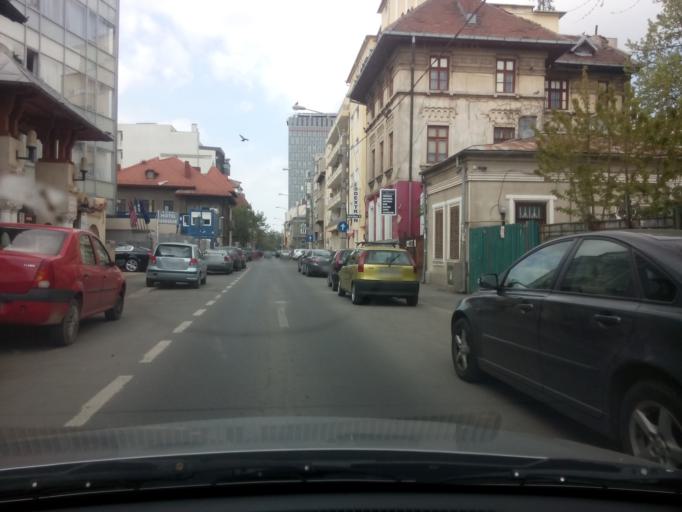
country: RO
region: Bucuresti
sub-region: Municipiul Bucuresti
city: Bucharest
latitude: 44.4499
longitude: 26.0962
